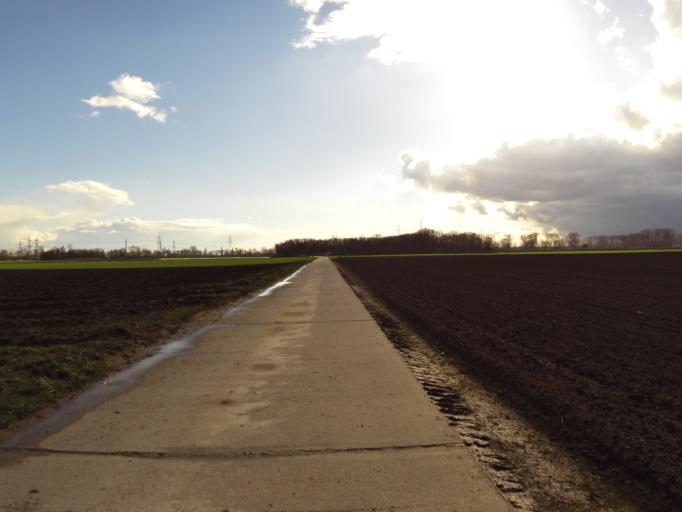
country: DE
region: Rheinland-Pfalz
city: Worms
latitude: 49.6816
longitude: 8.3801
